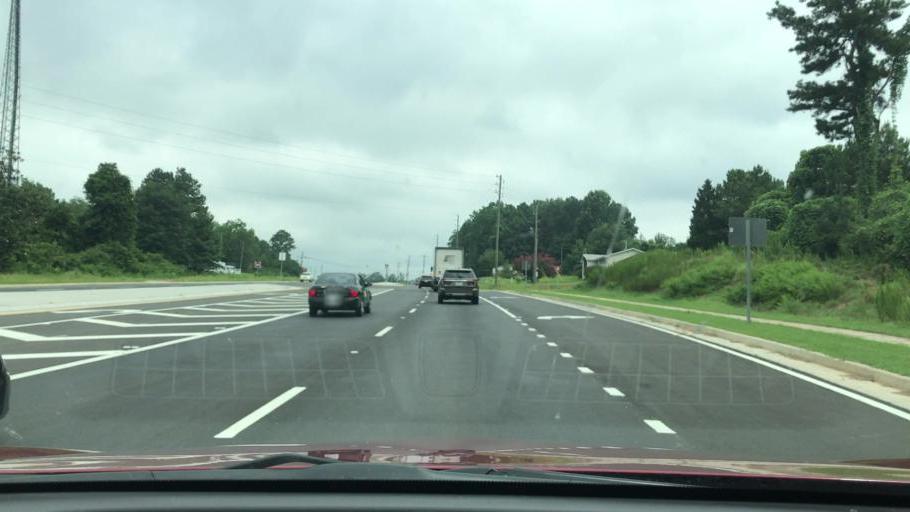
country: US
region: Georgia
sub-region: Forsyth County
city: Cumming
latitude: 34.1560
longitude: -84.1076
